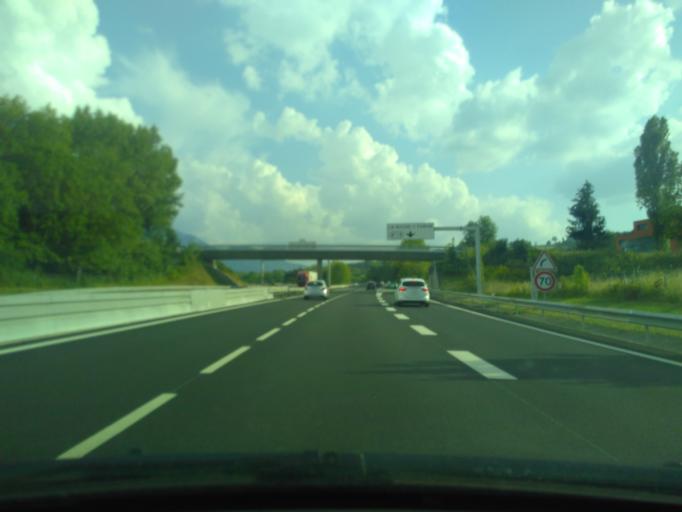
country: FR
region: Rhone-Alpes
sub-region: Departement de la Haute-Savoie
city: Etaux
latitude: 46.0736
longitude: 6.2906
